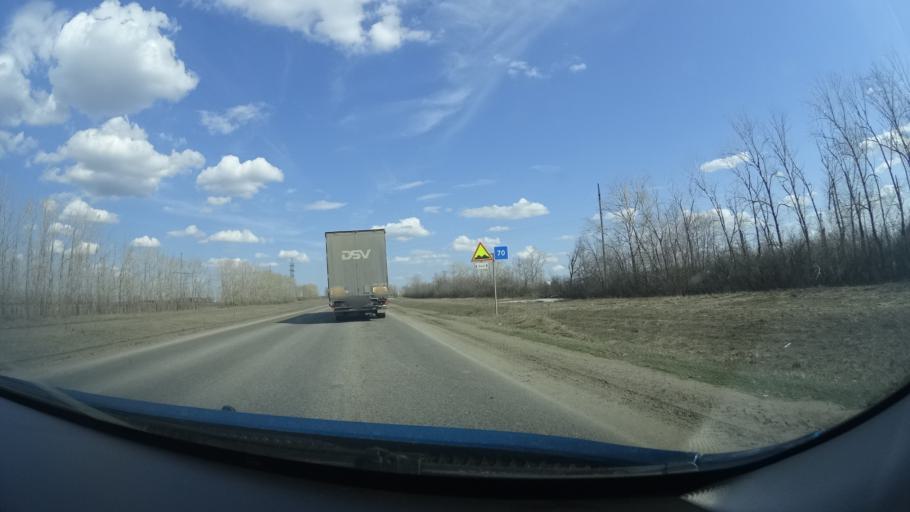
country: RU
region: Bashkortostan
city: Buzdyak
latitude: 54.6730
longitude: 54.7665
